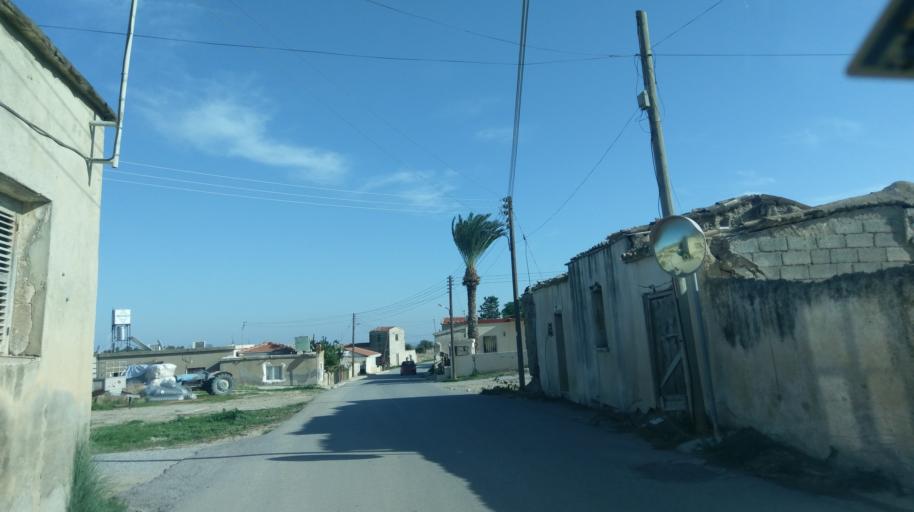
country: CY
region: Ammochostos
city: Trikomo
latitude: 35.3267
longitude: 33.8160
